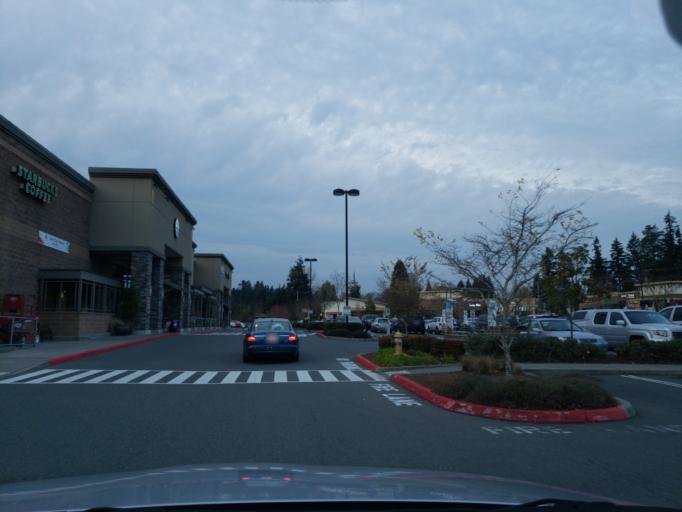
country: US
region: Washington
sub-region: King County
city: Bothell
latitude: 47.7785
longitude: -122.2199
